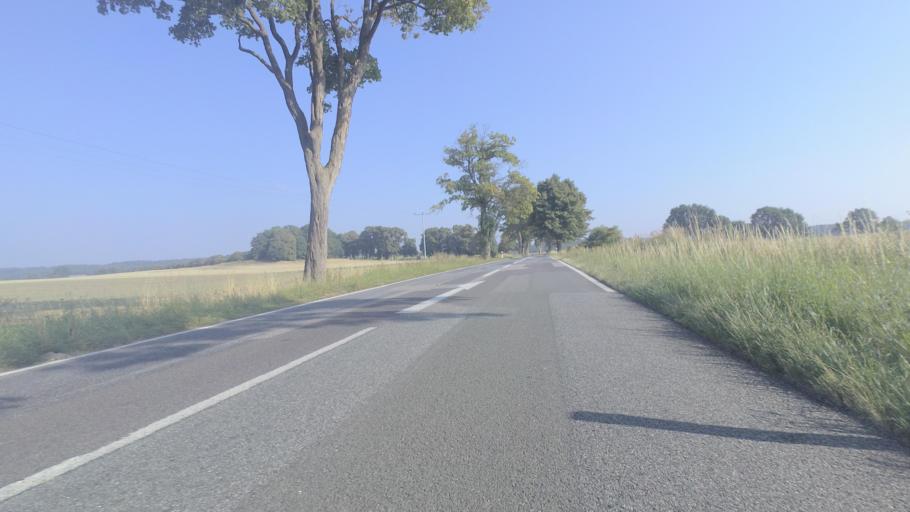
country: DE
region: Mecklenburg-Vorpommern
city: Malchow
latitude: 53.4360
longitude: 12.4344
